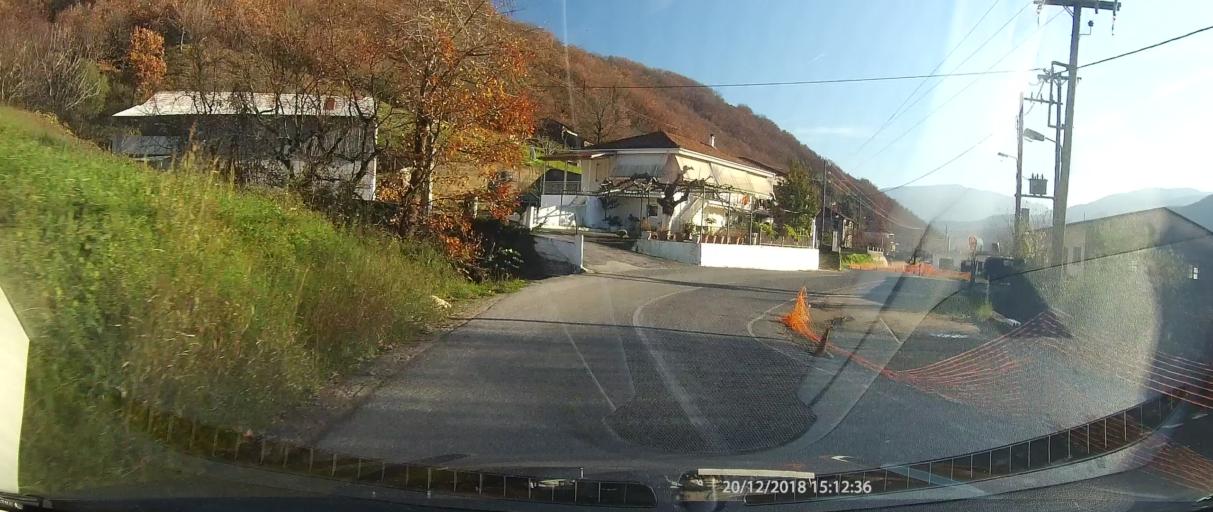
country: GR
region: Central Greece
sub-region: Nomos Fthiotidos
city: Makrakomi
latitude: 38.9411
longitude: 21.9633
